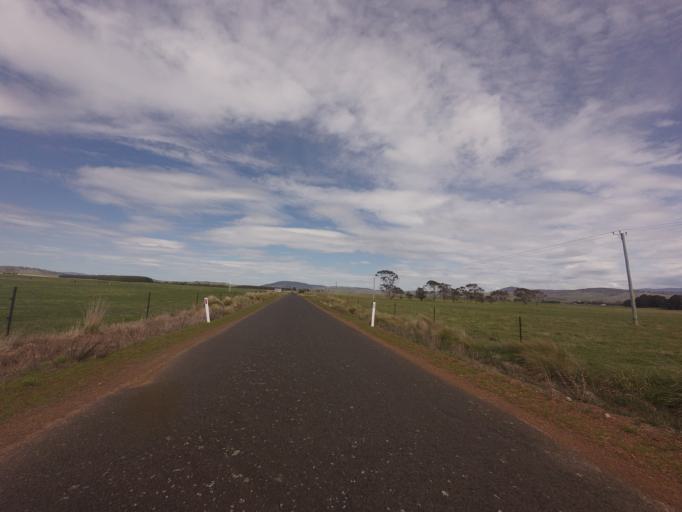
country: AU
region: Tasmania
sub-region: Northern Midlands
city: Evandale
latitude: -41.8513
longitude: 147.3400
